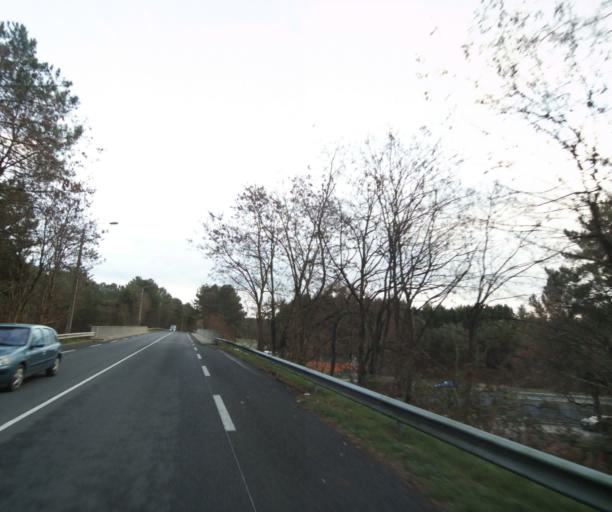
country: FR
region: Pays de la Loire
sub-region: Departement de la Sarthe
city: Ruaudin
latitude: 47.9695
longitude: 0.2346
